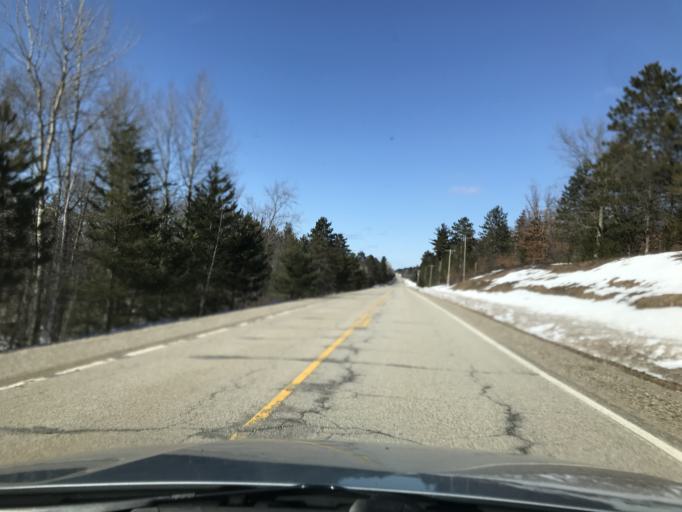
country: US
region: Wisconsin
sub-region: Marinette County
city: Niagara
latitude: 45.3588
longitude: -88.1008
